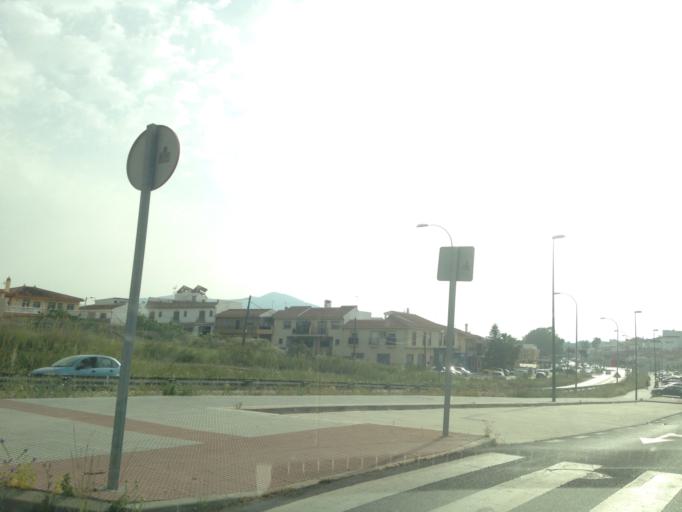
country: ES
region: Andalusia
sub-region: Provincia de Malaga
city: Estacion de Cartama
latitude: 36.7340
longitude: -4.5625
